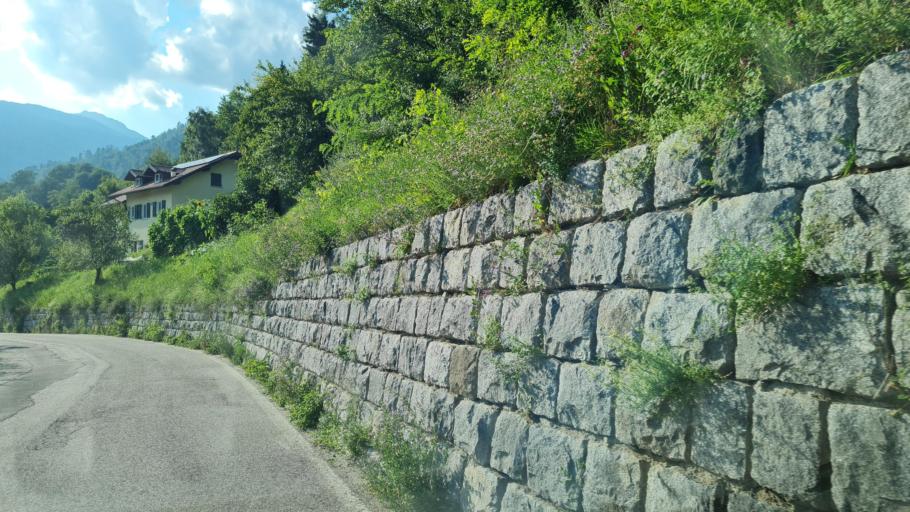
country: IT
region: Trentino-Alto Adige
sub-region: Provincia di Trento
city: Telve
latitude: 46.0758
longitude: 11.4772
